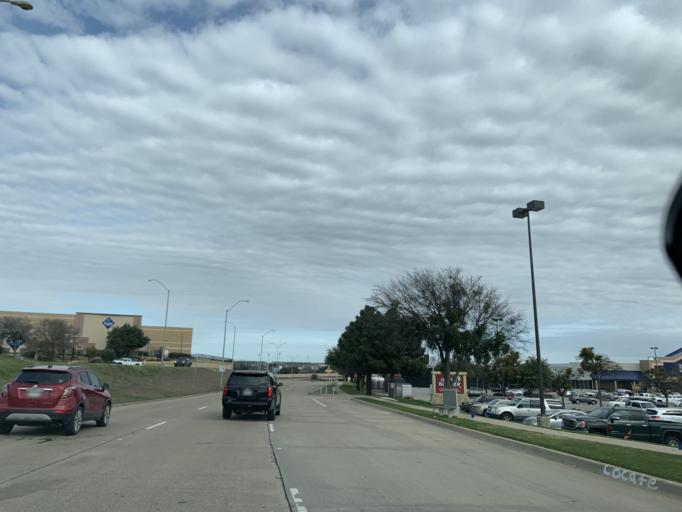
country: US
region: Texas
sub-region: Tarrant County
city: Benbrook
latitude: 32.6863
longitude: -97.4136
